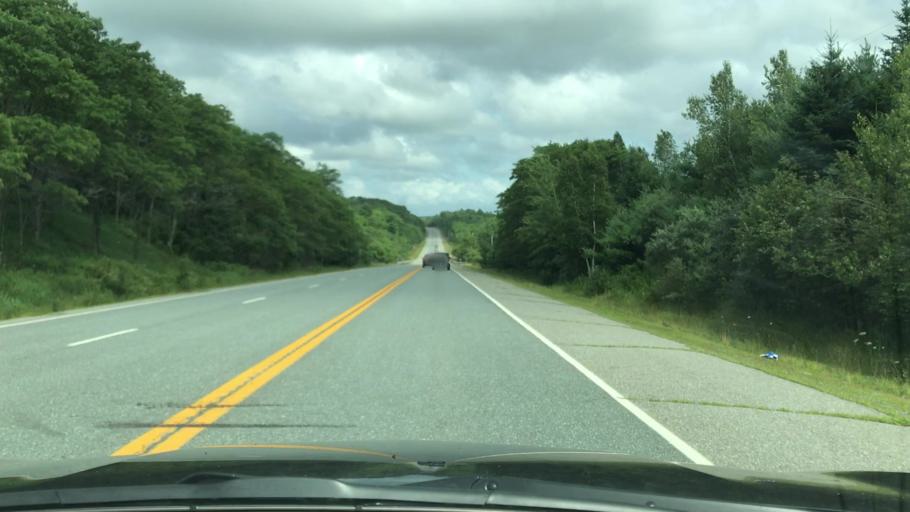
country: US
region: Maine
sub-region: Hancock County
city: Orland
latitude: 44.5666
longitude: -68.6154
